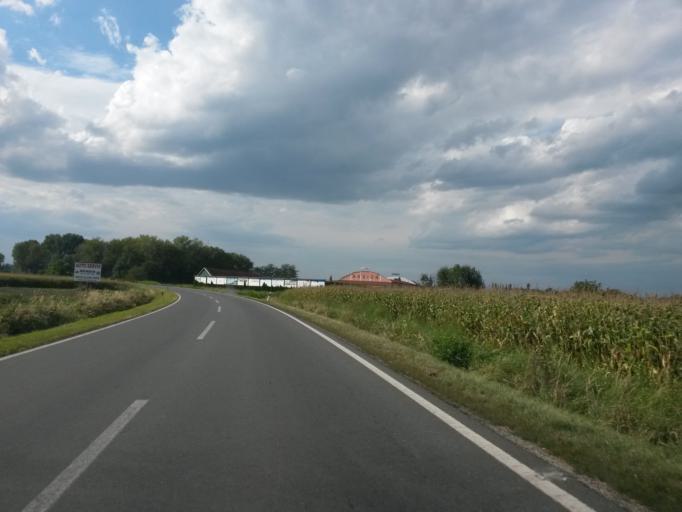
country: HR
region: Vukovarsko-Srijemska
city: Jarmina
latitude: 45.2861
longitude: 18.7587
